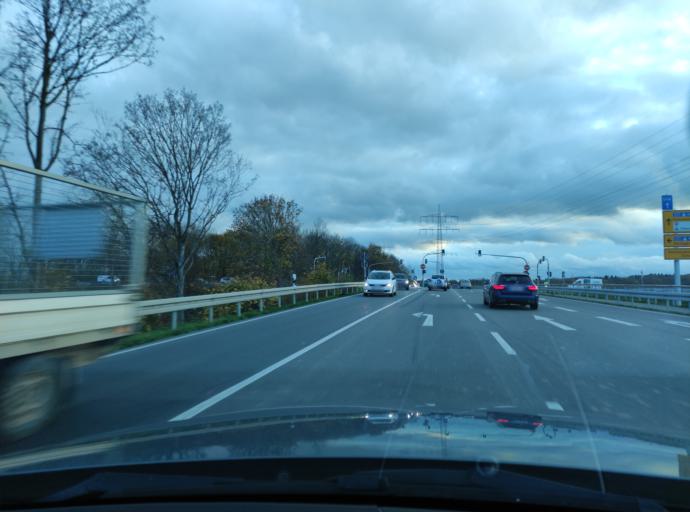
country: DE
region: North Rhine-Westphalia
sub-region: Regierungsbezirk Dusseldorf
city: Dormagen
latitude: 51.0946
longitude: 6.8020
